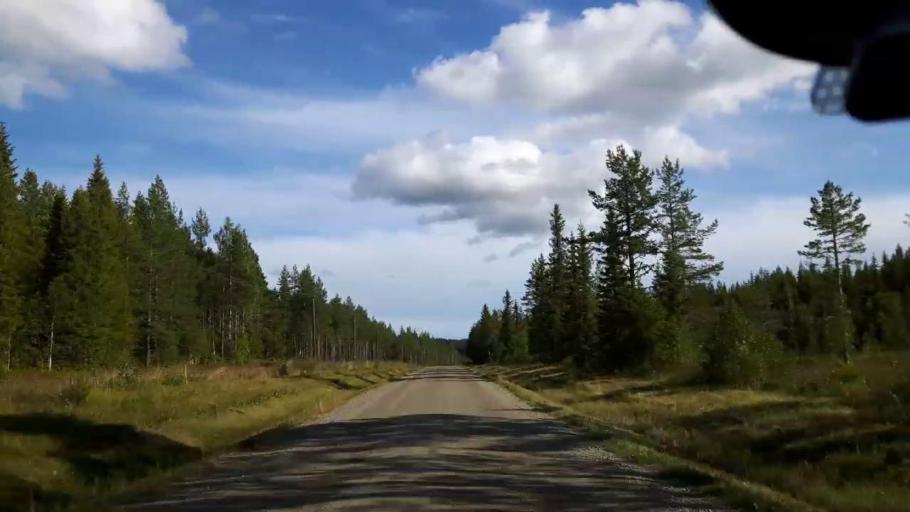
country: SE
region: Jaemtland
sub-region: Ragunda Kommun
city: Hammarstrand
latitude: 63.4299
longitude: 16.0476
